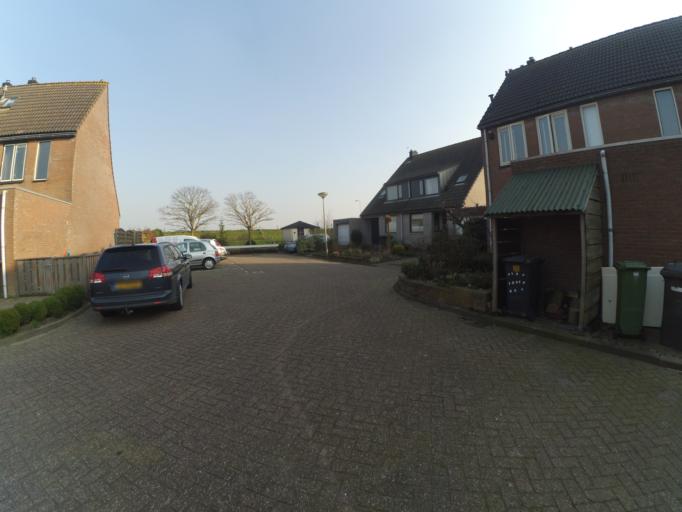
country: NL
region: South Holland
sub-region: Gemeente Spijkenisse
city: Spijkenisse
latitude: 51.8162
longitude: 4.2637
